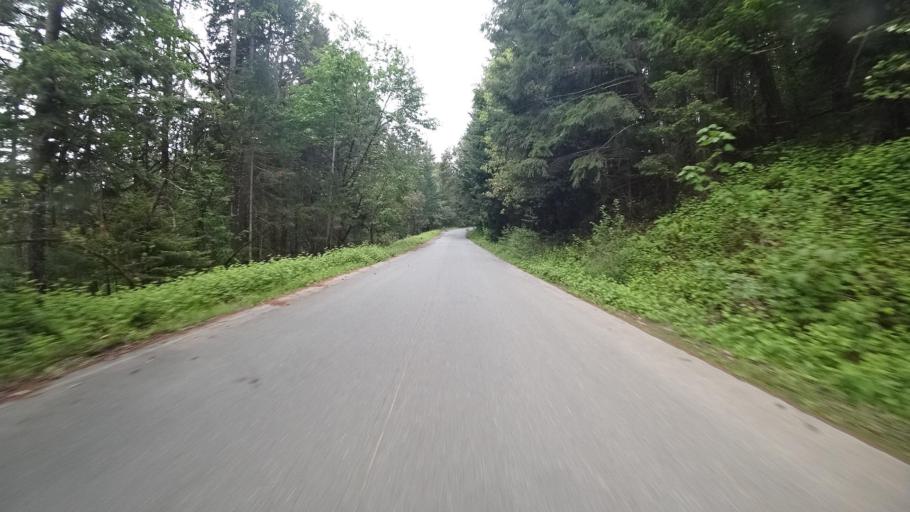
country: US
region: California
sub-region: Humboldt County
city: Willow Creek
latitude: 41.1189
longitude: -123.7310
